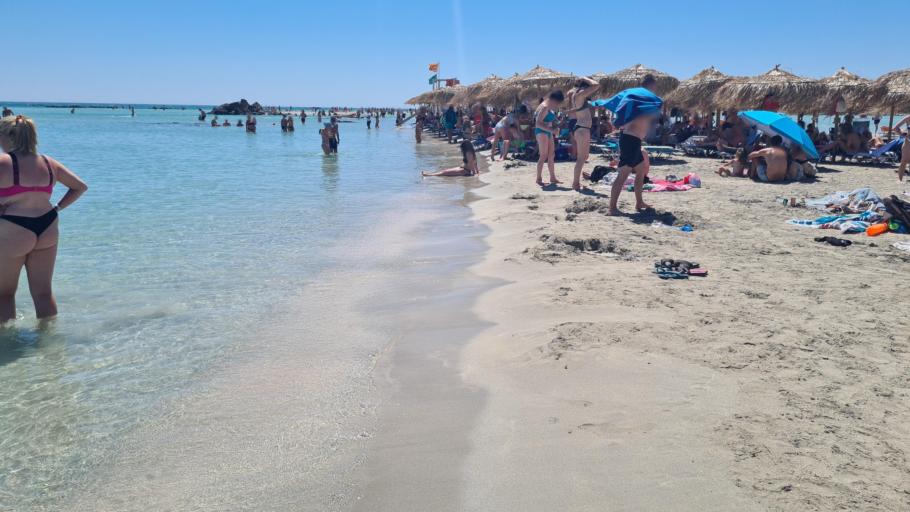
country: GR
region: Crete
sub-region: Nomos Chanias
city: Palaiochora
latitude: 35.2710
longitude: 23.5417
